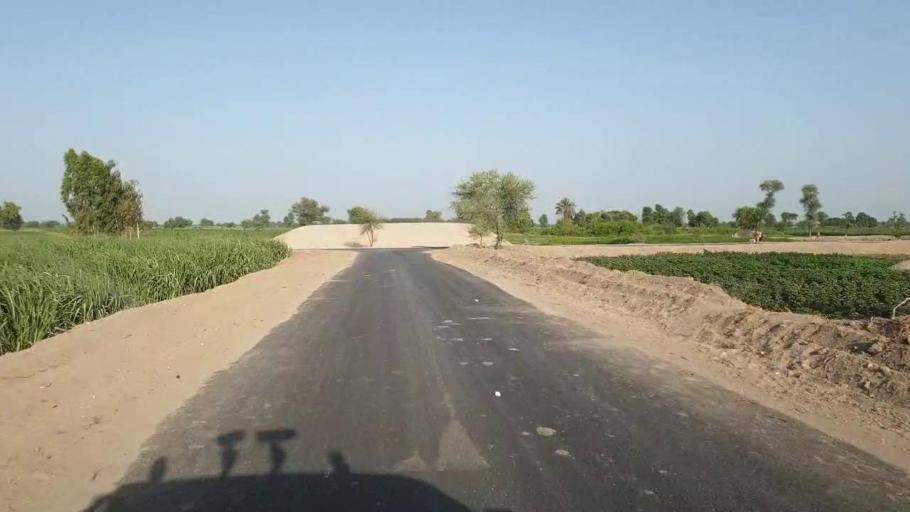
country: PK
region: Sindh
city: Jam Sahib
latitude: 26.3476
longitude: 68.5683
